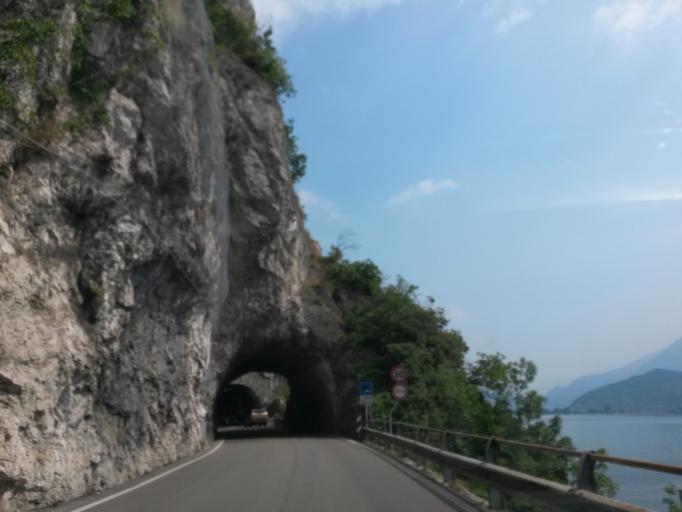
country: IT
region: Trentino-Alto Adige
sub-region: Provincia di Trento
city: Riva del Garda
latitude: 45.8593
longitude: 10.8327
